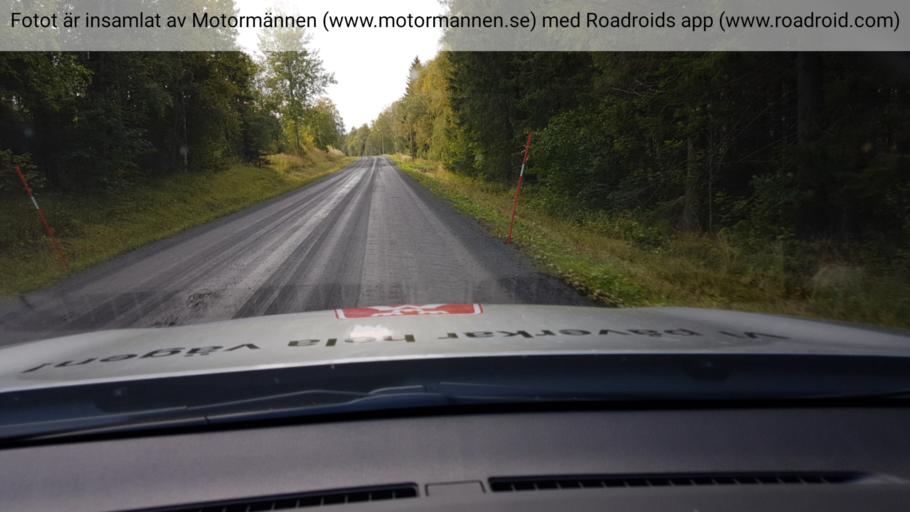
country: SE
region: Jaemtland
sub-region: Stroemsunds Kommun
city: Stroemsund
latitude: 64.1319
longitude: 15.7807
